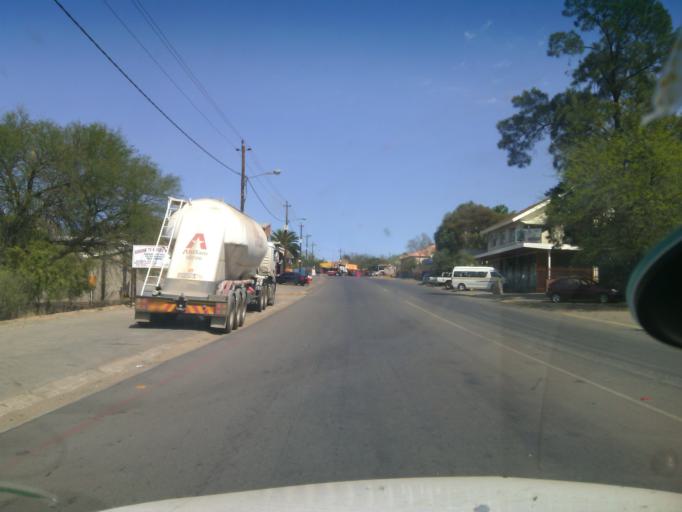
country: ZA
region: Northern Cape
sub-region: Frances Baard District Municipality
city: Barkly West
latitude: -28.5373
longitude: 24.5226
